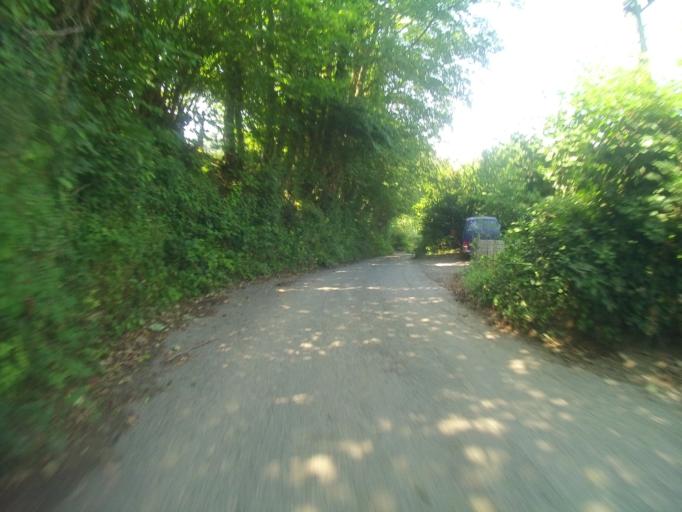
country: GB
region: England
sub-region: Devon
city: Dartmouth
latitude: 50.3556
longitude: -3.6000
